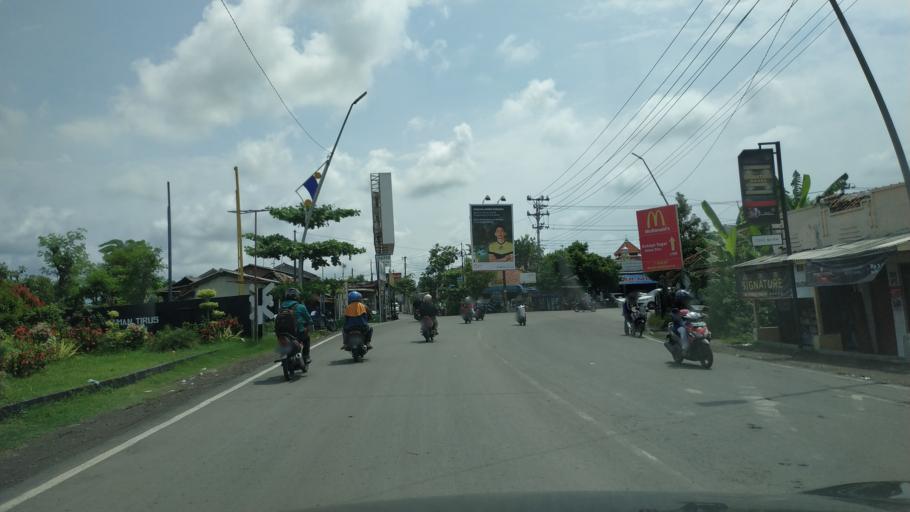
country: ID
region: Central Java
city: Tegal
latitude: -6.8833
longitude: 109.1267
